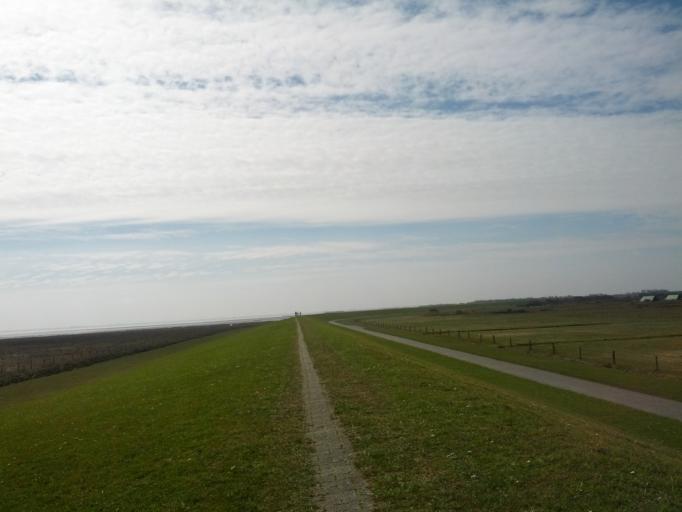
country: DE
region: Lower Saxony
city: Langeoog
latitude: 53.7487
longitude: 7.5105
